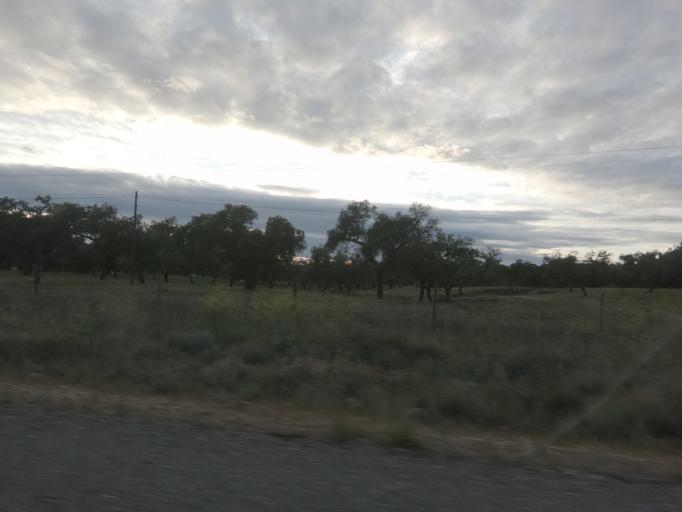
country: ES
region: Extremadura
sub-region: Provincia de Badajoz
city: Puebla de Obando
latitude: 39.1482
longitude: -6.6517
